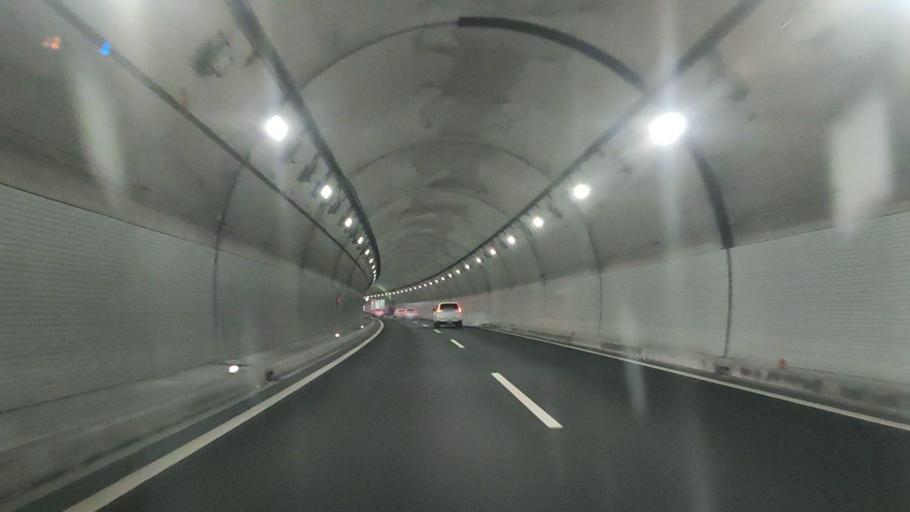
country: JP
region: Fukuoka
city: Kanda
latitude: 33.8026
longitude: 130.9469
